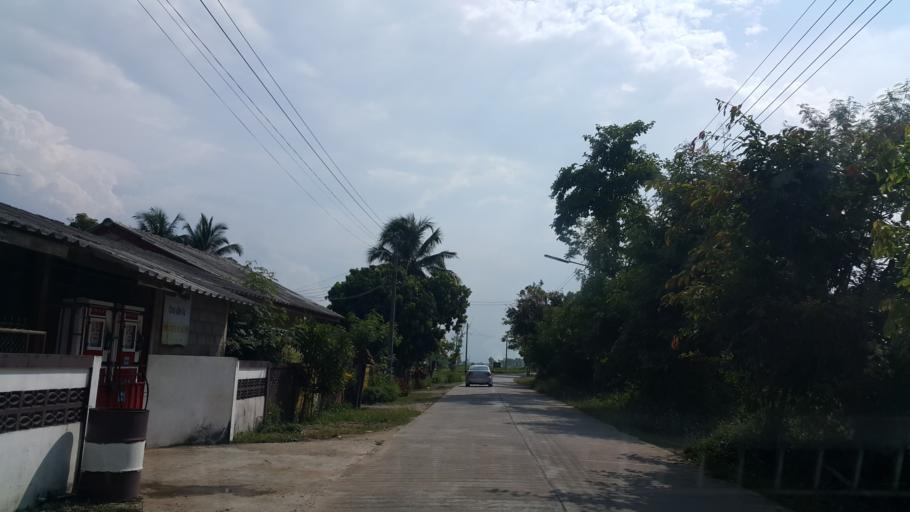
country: TH
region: Chiang Rai
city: Wiang Chai
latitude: 19.9347
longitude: 99.9343
